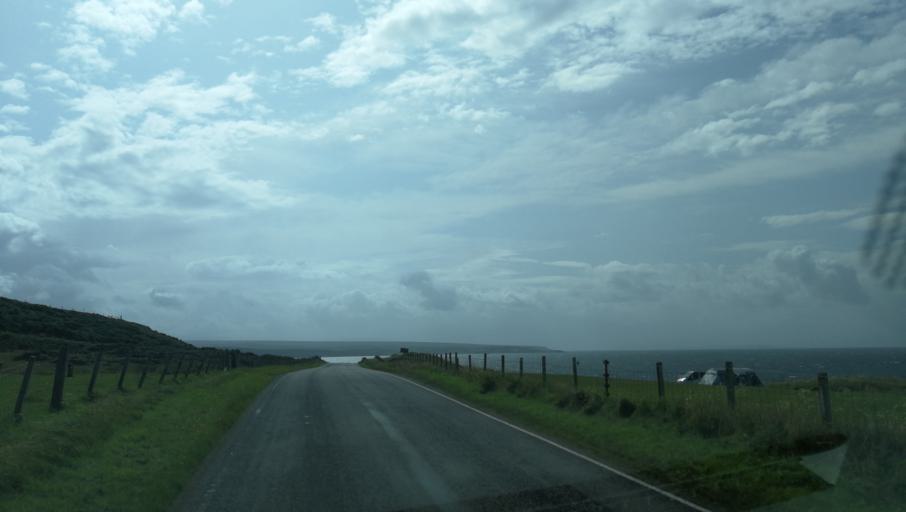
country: GB
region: Scotland
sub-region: Highland
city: Portree
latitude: 57.7366
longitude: -5.7634
